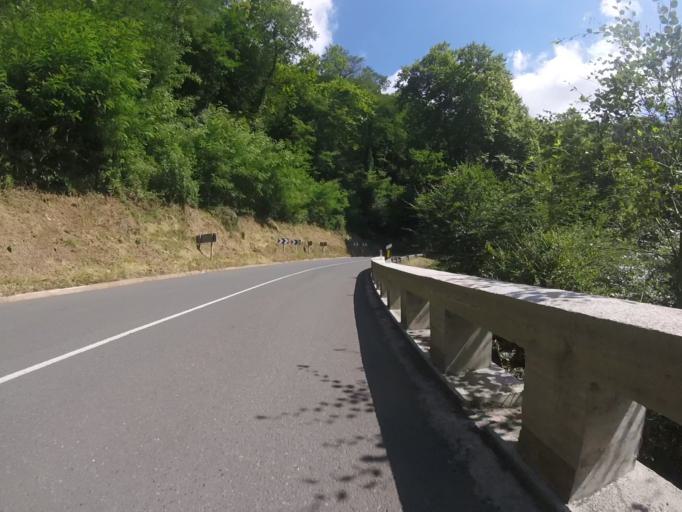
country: ES
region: Basque Country
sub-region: Provincia de Guipuzcoa
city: Azpeitia
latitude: 43.1792
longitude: -2.2470
